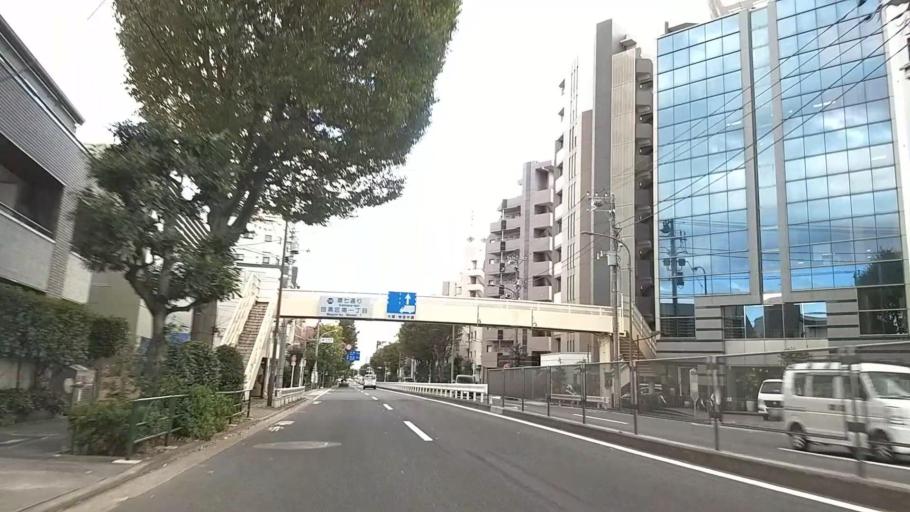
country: JP
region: Tokyo
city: Tokyo
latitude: 35.6112
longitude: 139.6901
